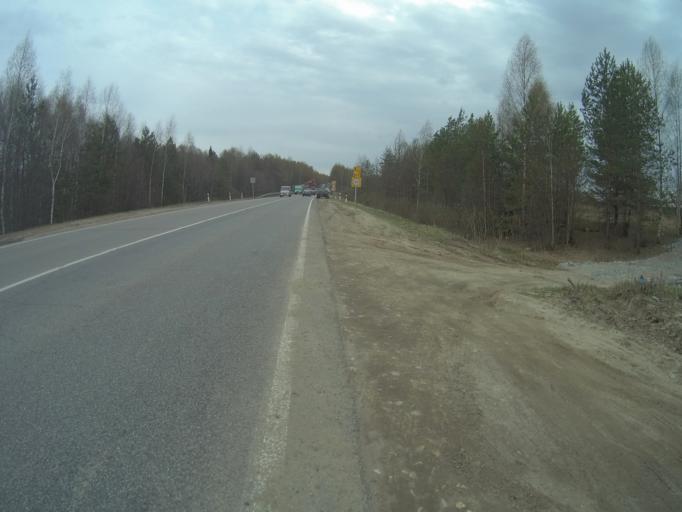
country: RU
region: Vladimir
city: Golovino
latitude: 55.9482
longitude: 40.5792
